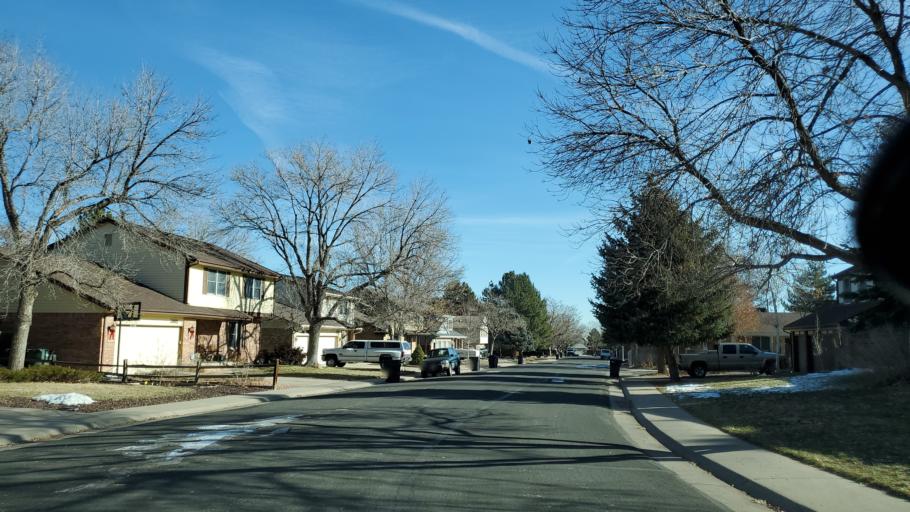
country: US
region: Colorado
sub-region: Adams County
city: Northglenn
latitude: 39.9206
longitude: -104.9537
